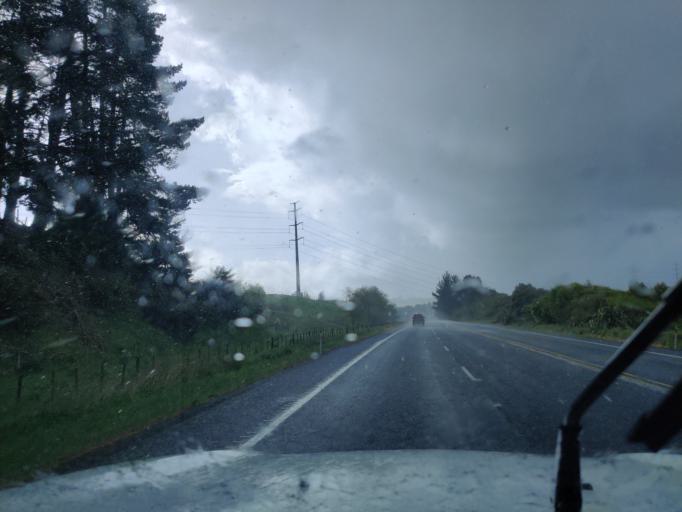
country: NZ
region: Waikato
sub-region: Waipa District
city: Cambridge
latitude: -37.9486
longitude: 175.6153
